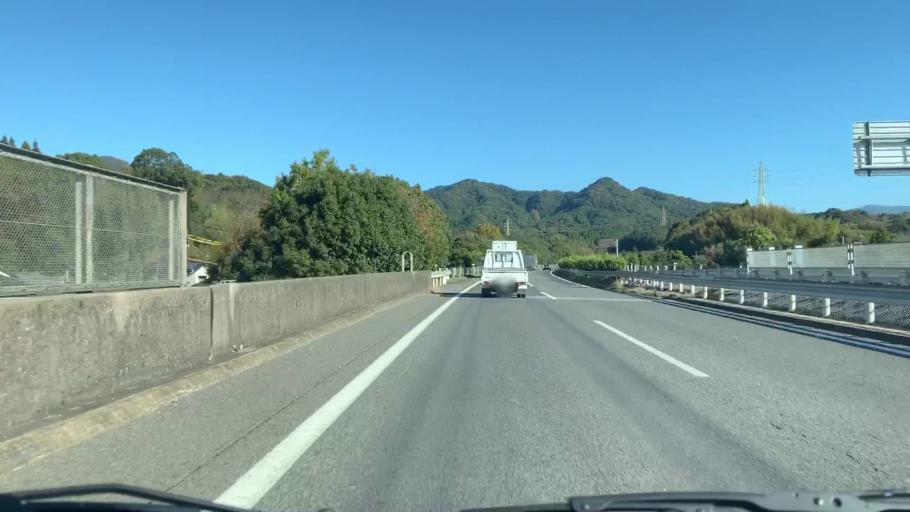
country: JP
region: Saga Prefecture
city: Takeocho-takeo
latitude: 33.2231
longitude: 130.0498
